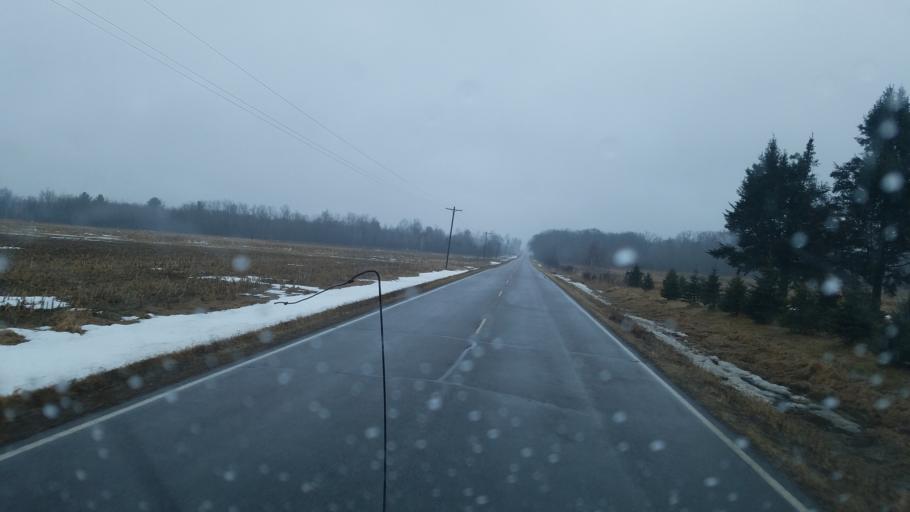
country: US
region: Wisconsin
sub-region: Wood County
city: Marshfield
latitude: 44.4865
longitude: -90.2797
